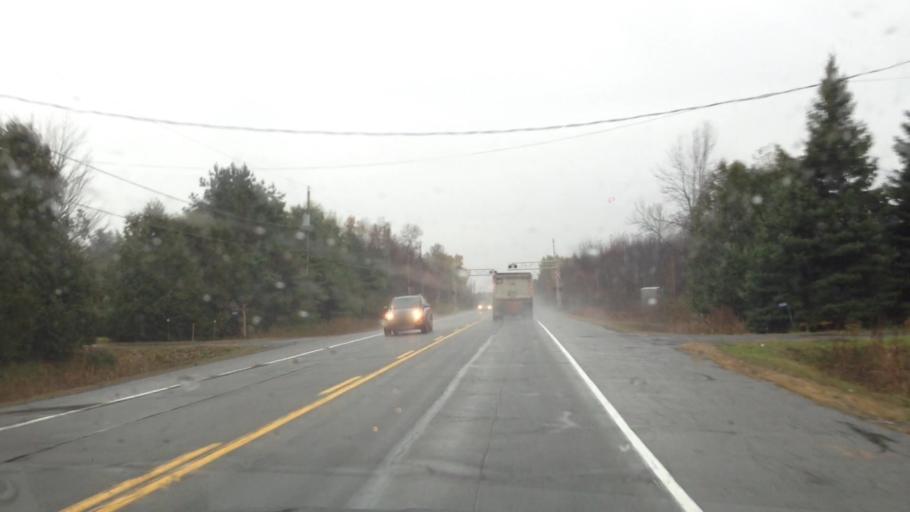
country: CA
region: Ontario
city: Clarence-Rockland
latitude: 45.3564
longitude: -75.3714
